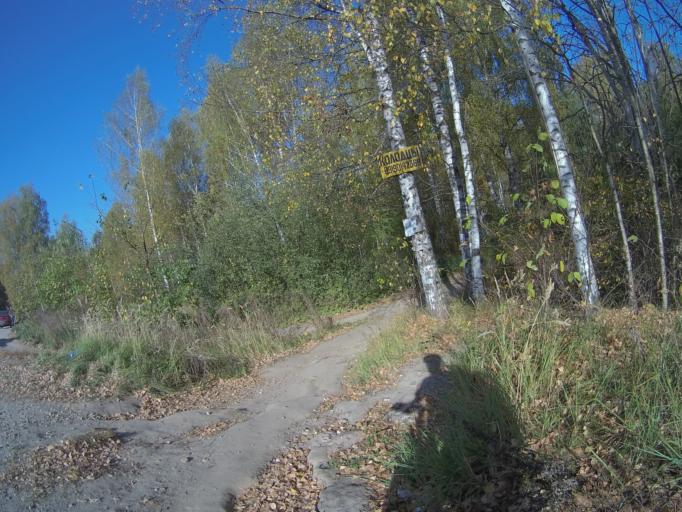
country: RU
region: Vladimir
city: Raduzhnyy
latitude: 56.0018
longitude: 40.2807
